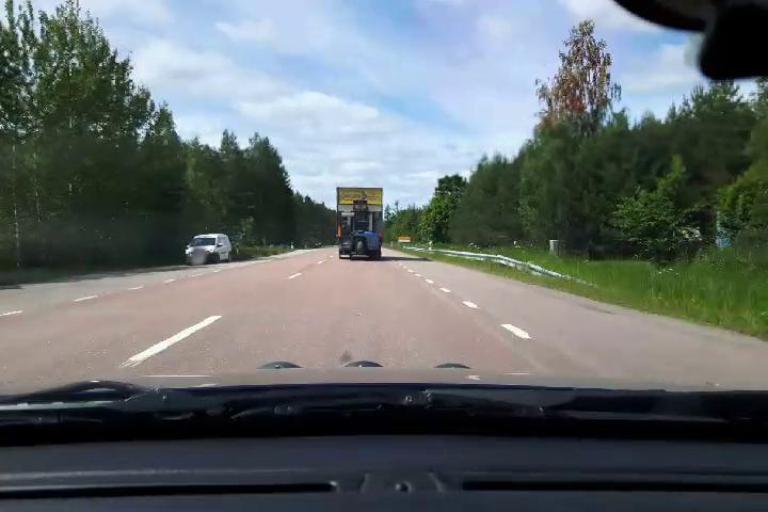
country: SE
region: Uppsala
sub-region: Osthammars Kommun
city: Bjorklinge
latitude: 60.1104
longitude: 17.5332
